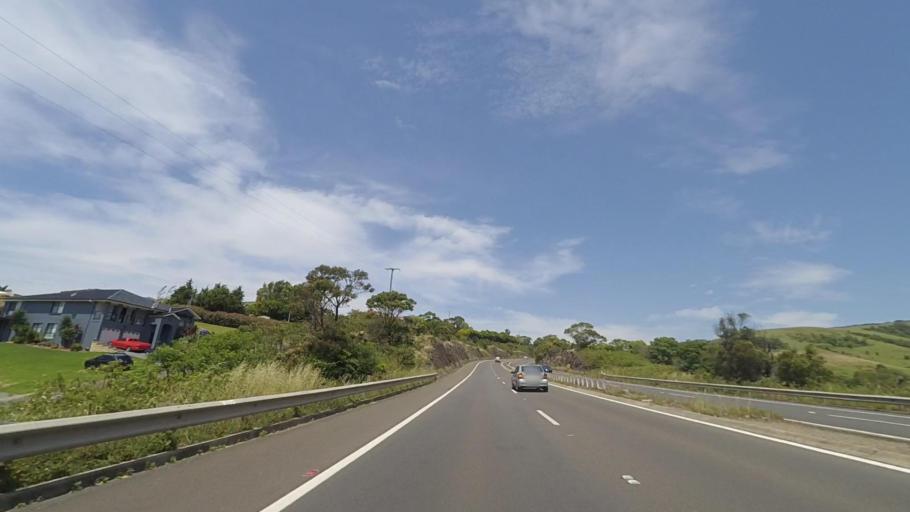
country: AU
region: New South Wales
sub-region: Kiama
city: Kiama
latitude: -34.6913
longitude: 150.8442
